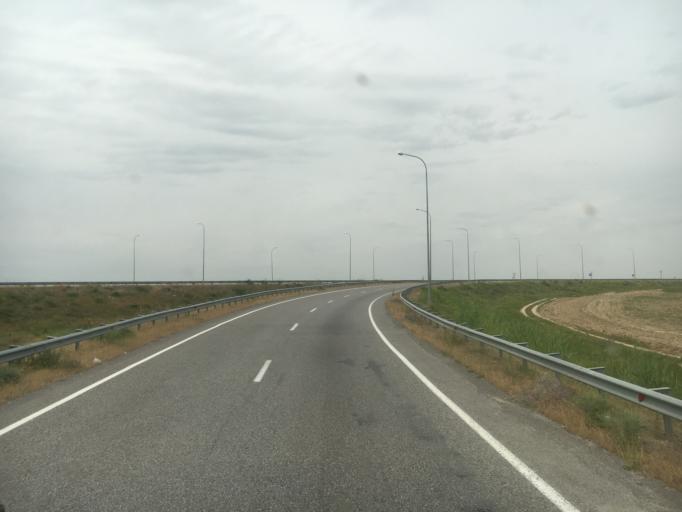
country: KZ
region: Ongtustik Qazaqstan
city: Temirlanovka
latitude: 42.5303
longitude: 69.3440
